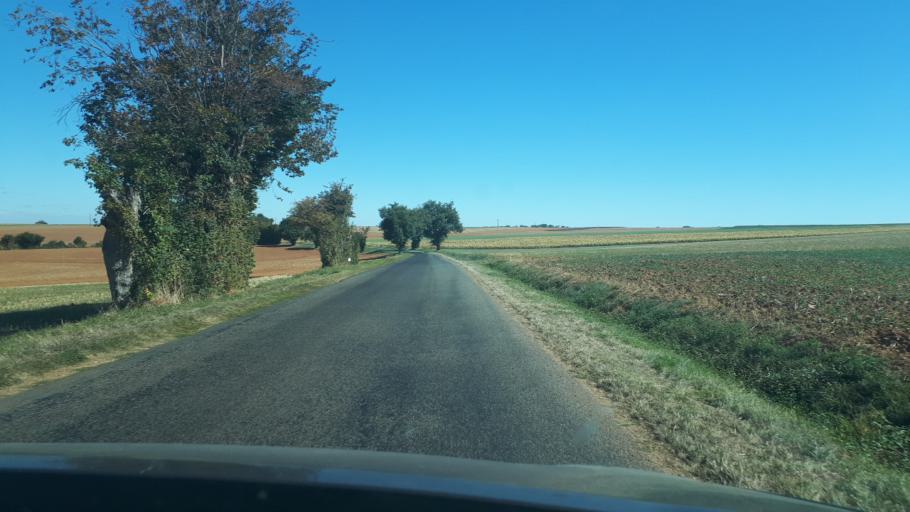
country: FR
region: Centre
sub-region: Departement du Cher
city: Sancerre
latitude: 47.3177
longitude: 2.7678
